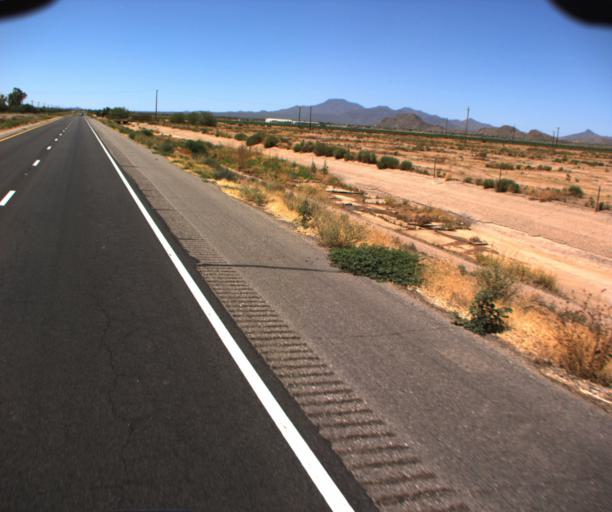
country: US
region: Arizona
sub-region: Pinal County
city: Maricopa
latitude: 32.9036
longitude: -112.0496
